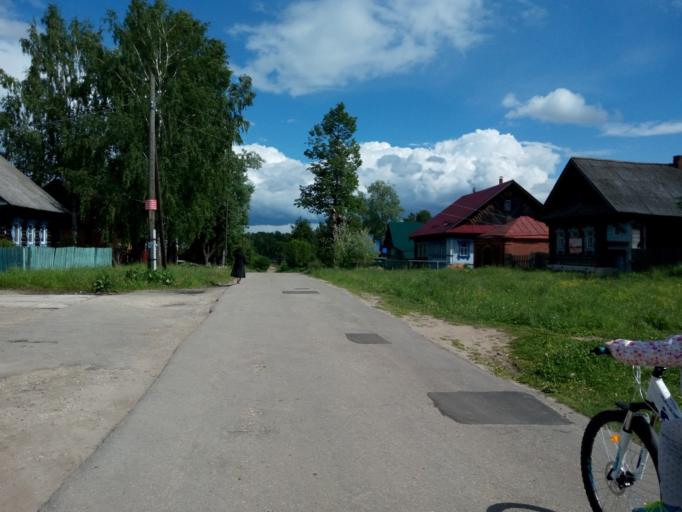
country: RU
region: Nizjnij Novgorod
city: Voskresenskoye
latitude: 56.7811
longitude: 45.5234
